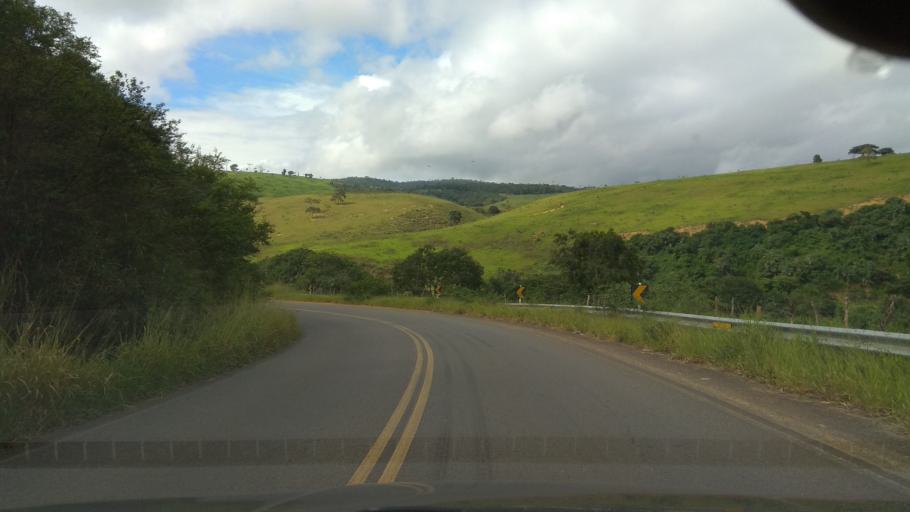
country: BR
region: Bahia
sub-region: Ubaira
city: Ubaira
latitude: -13.2624
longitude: -39.7095
